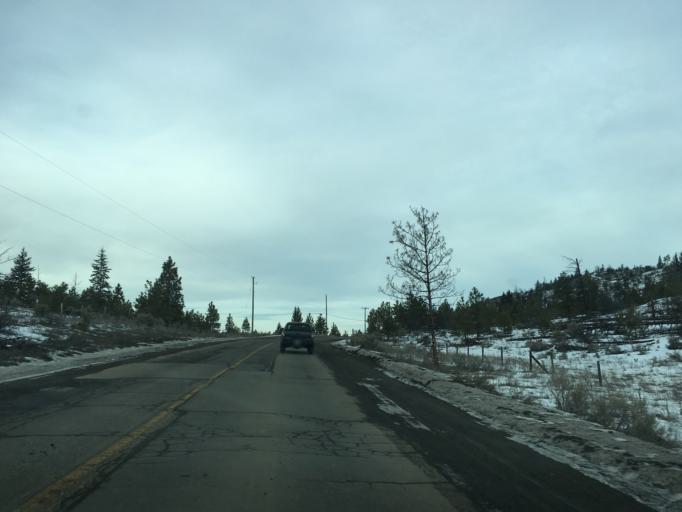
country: CA
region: British Columbia
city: Kamloops
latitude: 50.6386
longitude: -120.4492
